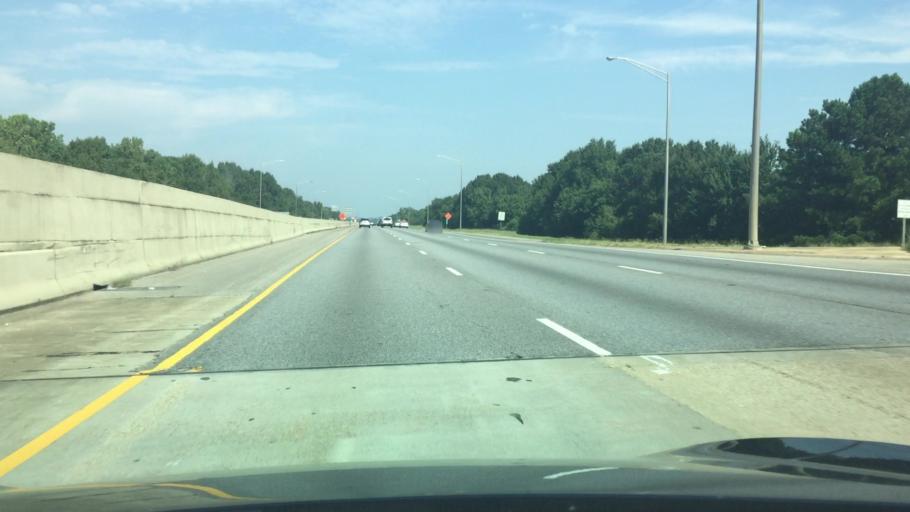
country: US
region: Alabama
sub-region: Montgomery County
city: Montgomery
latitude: 32.3910
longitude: -86.3250
